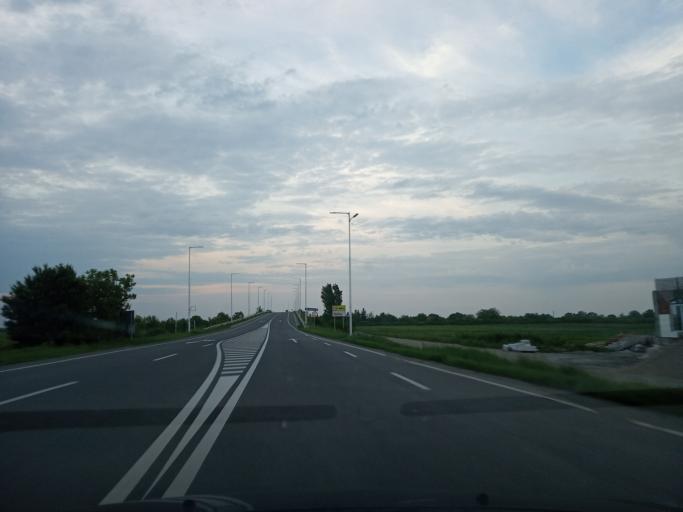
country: RO
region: Timis
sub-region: Comuna Voiteg
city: Voiteg
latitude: 45.4607
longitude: 21.2352
